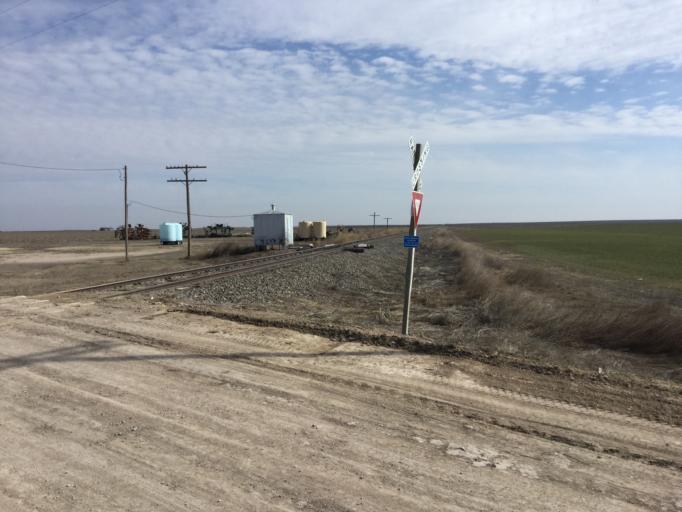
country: US
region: Kansas
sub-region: Scott County
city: Scott City
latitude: 38.5034
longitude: -100.8520
